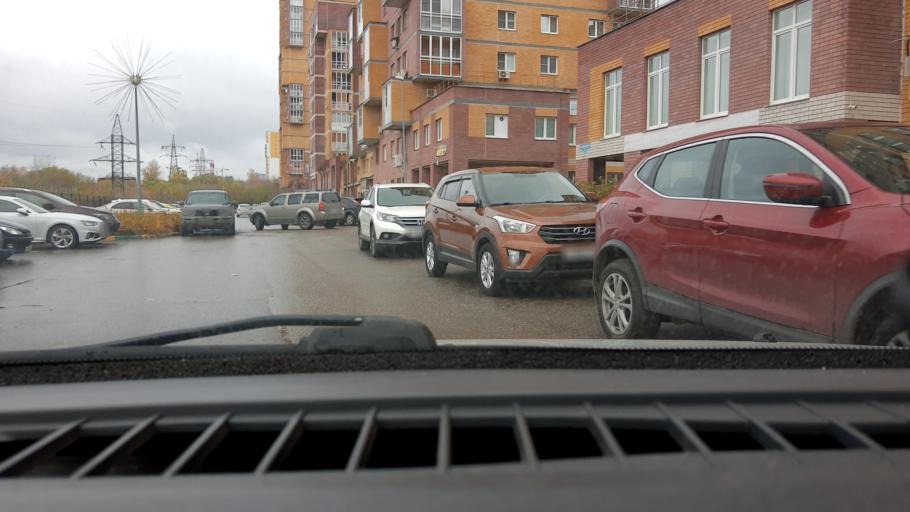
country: RU
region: Nizjnij Novgorod
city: Nizhniy Novgorod
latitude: 56.3073
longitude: 44.0313
